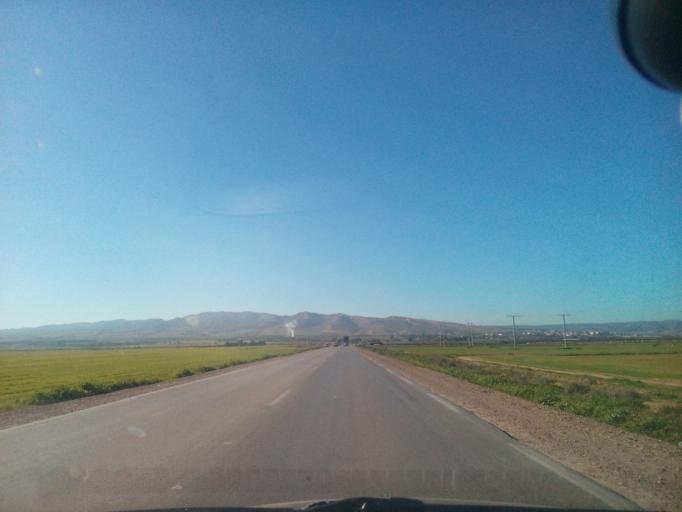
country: DZ
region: Relizane
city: Relizane
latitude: 35.8976
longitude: 0.5532
